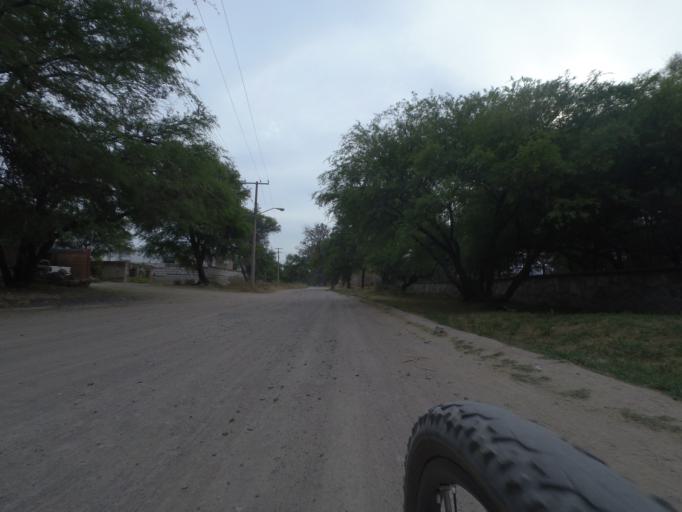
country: MX
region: Aguascalientes
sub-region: Aguascalientes
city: La Loma de los Negritos
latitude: 21.8541
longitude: -102.3562
